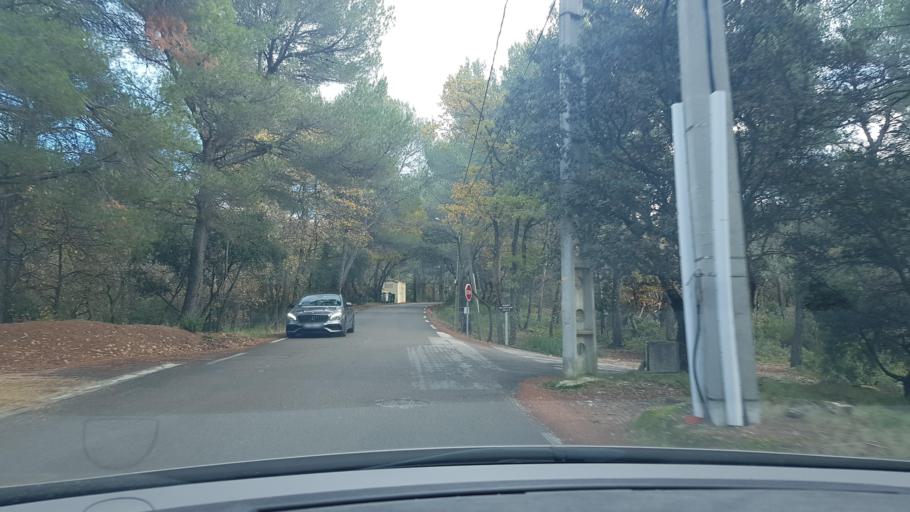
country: FR
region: Provence-Alpes-Cote d'Azur
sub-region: Departement des Bouches-du-Rhone
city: Simiane-Collongue
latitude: 43.4213
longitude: 5.4539
